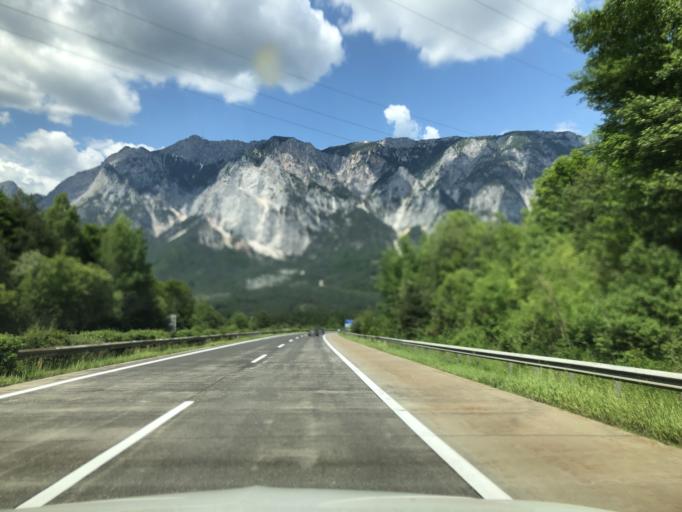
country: AT
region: Carinthia
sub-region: Politischer Bezirk Villach Land
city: Hohenthurn
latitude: 46.5589
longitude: 13.6849
